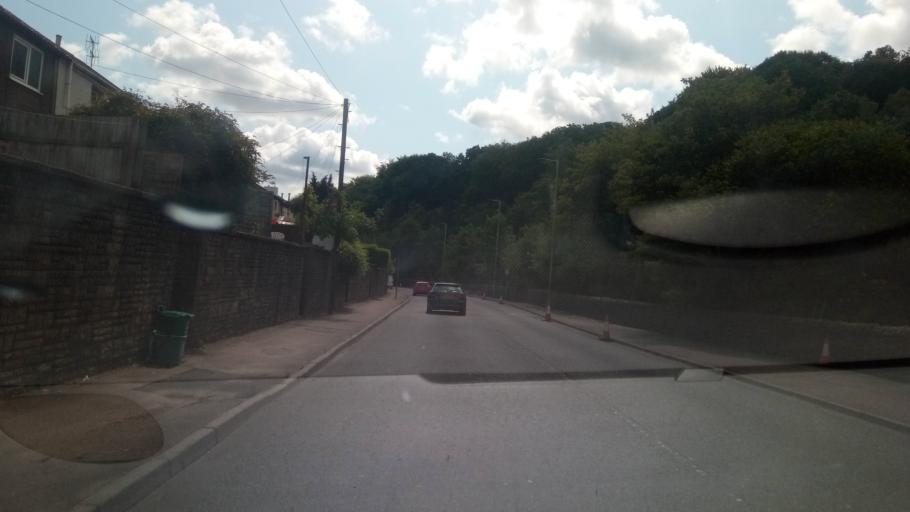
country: GB
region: Wales
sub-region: Rhondda Cynon Taf
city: Pontypridd
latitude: 51.6058
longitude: -3.3585
